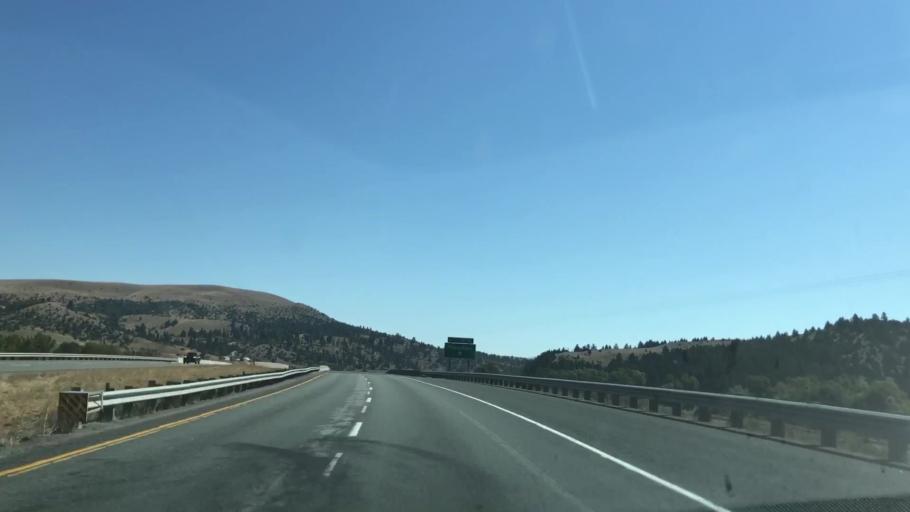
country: US
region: Montana
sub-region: Powell County
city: Deer Lodge
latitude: 46.5570
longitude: -112.8753
